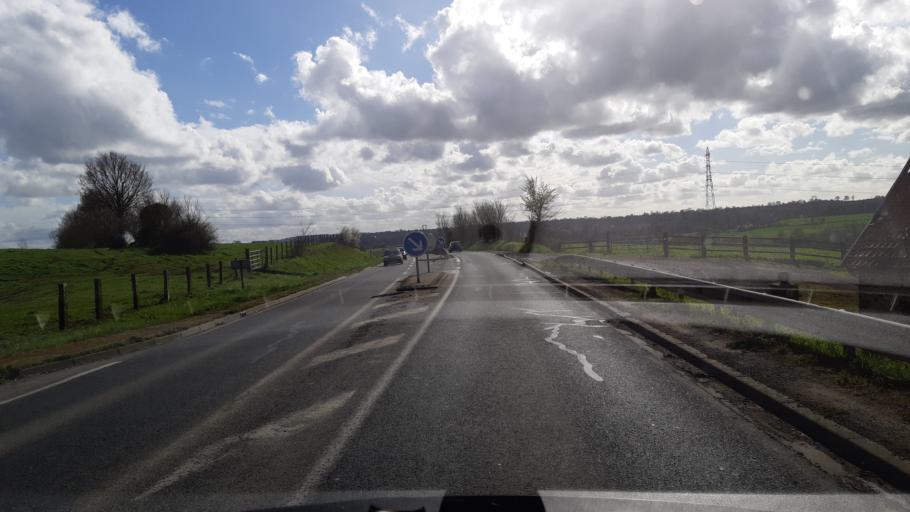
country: FR
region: Lower Normandy
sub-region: Departement de la Manche
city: Agneaux
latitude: 49.0989
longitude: -1.1194
